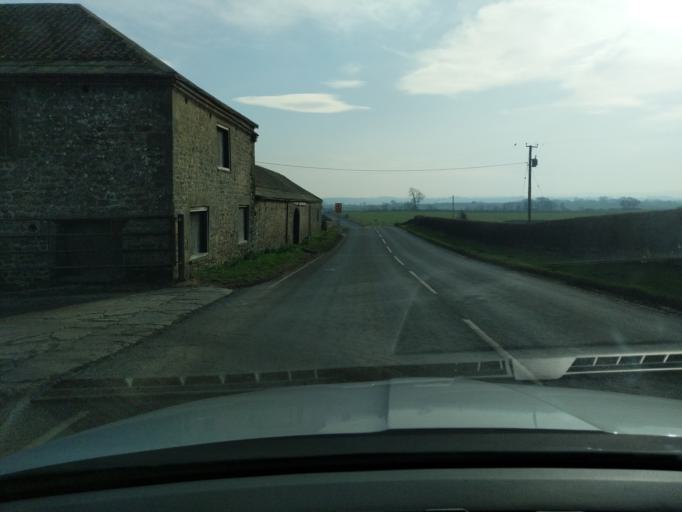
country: GB
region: England
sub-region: North Yorkshire
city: Catterick Garrison
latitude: 54.3362
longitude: -1.6861
